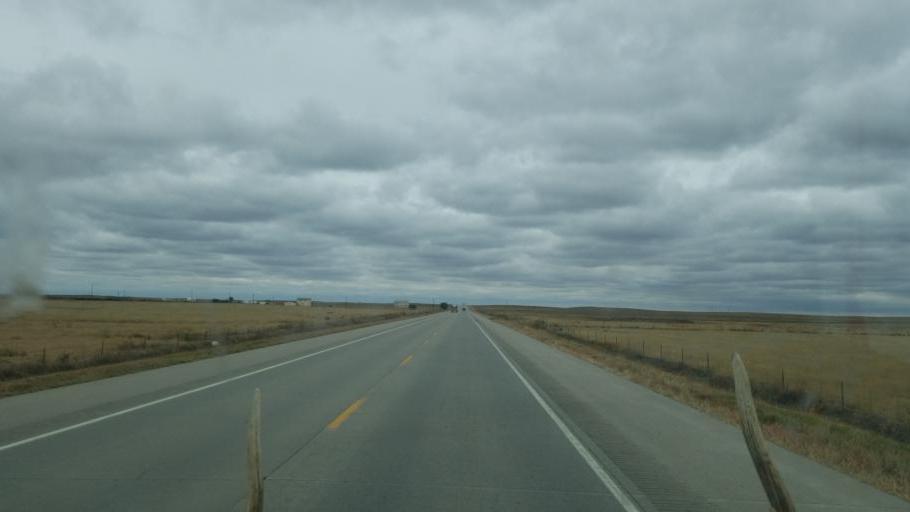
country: US
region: Colorado
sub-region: Kiowa County
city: Eads
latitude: 38.4933
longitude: -102.7857
